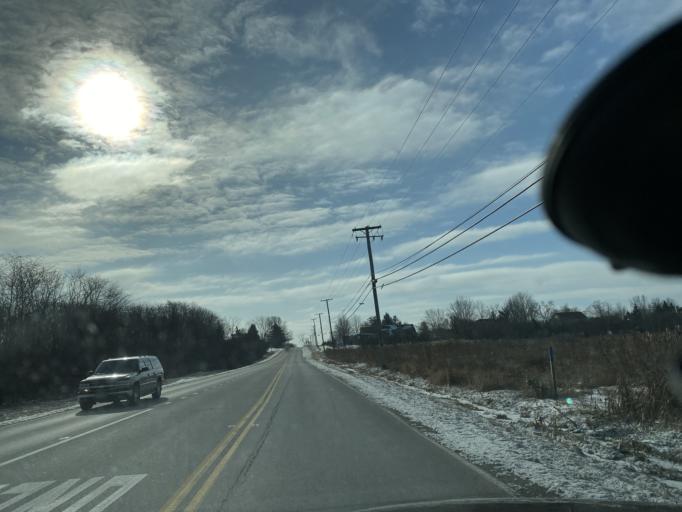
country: US
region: Illinois
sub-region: Will County
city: Goodings Grove
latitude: 41.6650
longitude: -87.9321
